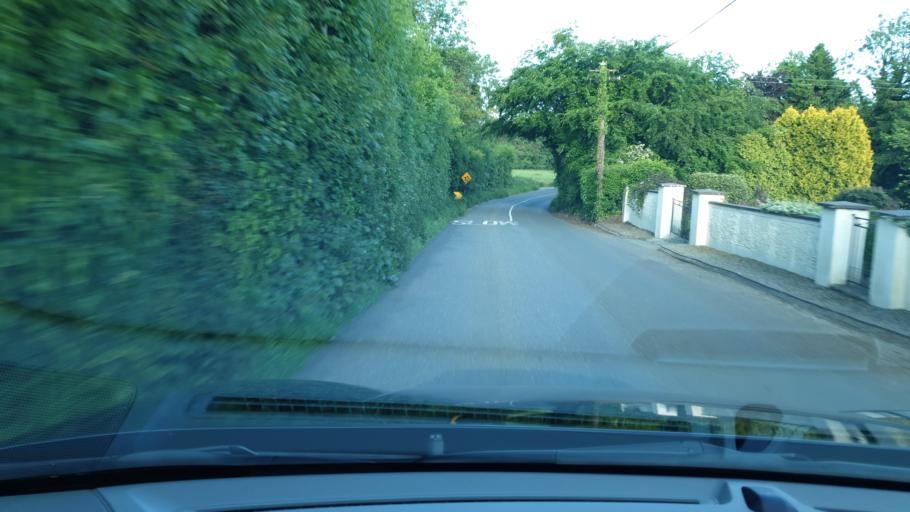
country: IE
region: Leinster
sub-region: An Mhi
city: Ashbourne
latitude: 53.5338
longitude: -6.3135
